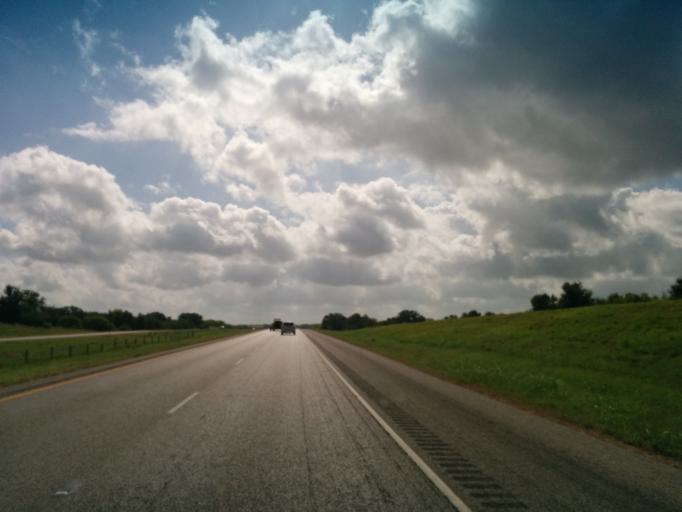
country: US
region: Texas
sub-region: Gonzales County
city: Waelder
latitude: 29.6644
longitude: -97.3595
